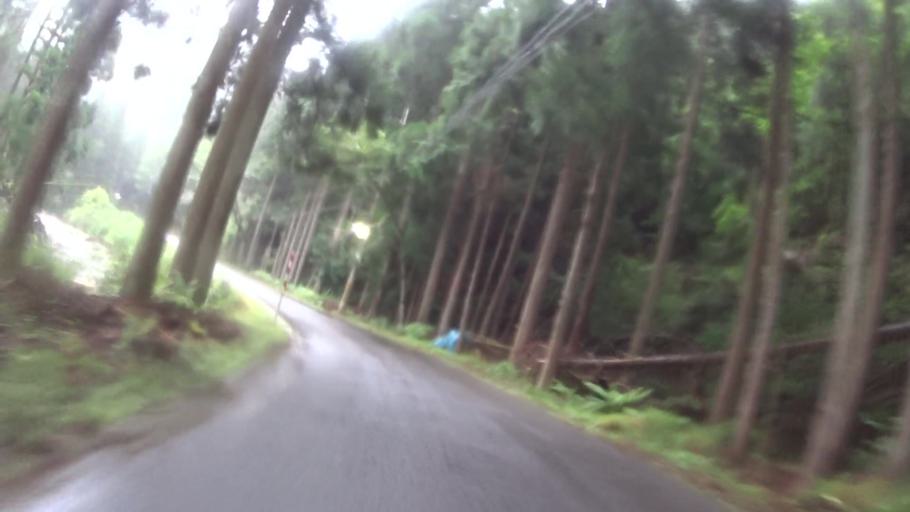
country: JP
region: Shiga Prefecture
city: Kitahama
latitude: 35.2562
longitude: 135.7669
